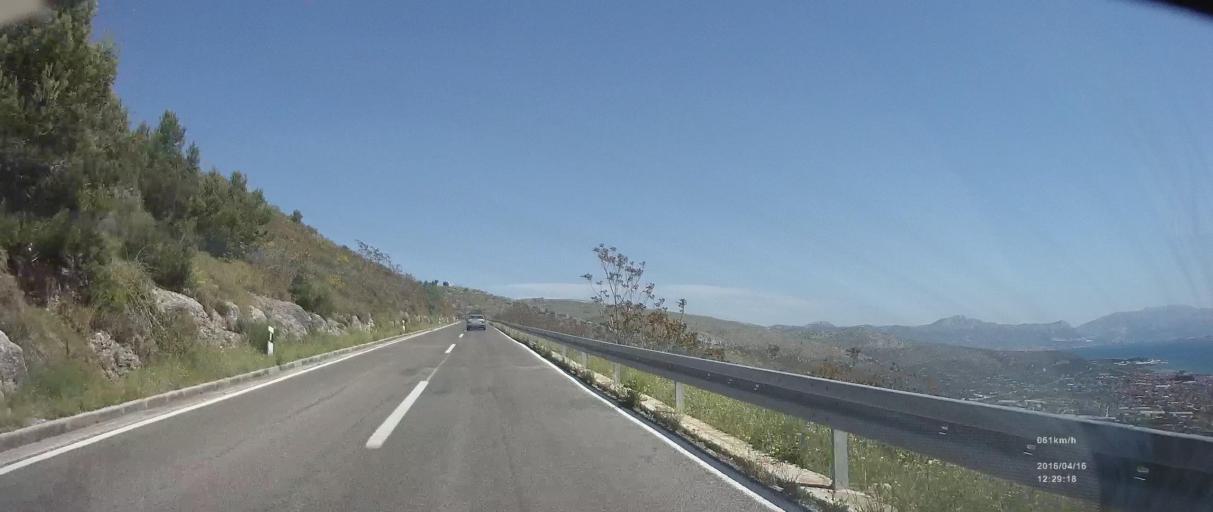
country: HR
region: Splitsko-Dalmatinska
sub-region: Grad Trogir
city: Trogir
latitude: 43.5225
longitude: 16.2179
